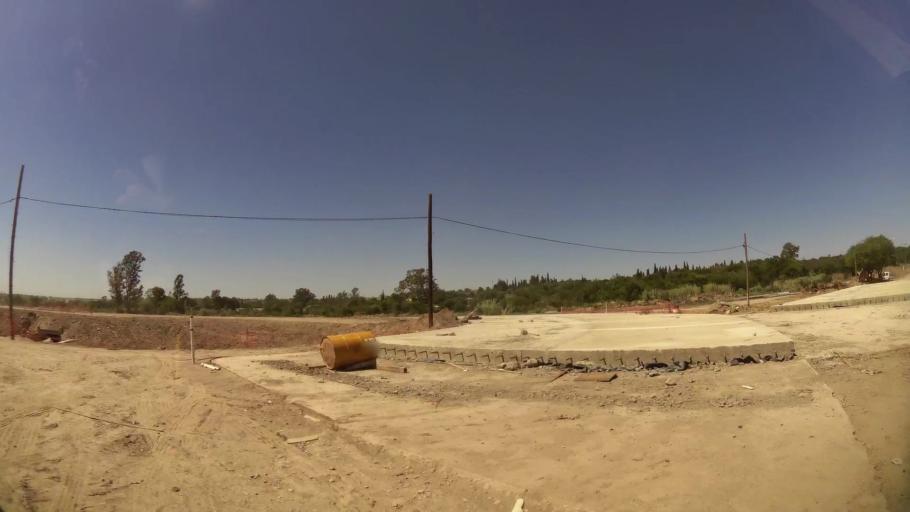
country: AR
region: Cordoba
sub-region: Departamento de Capital
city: Cordoba
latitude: -31.4080
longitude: -64.1257
